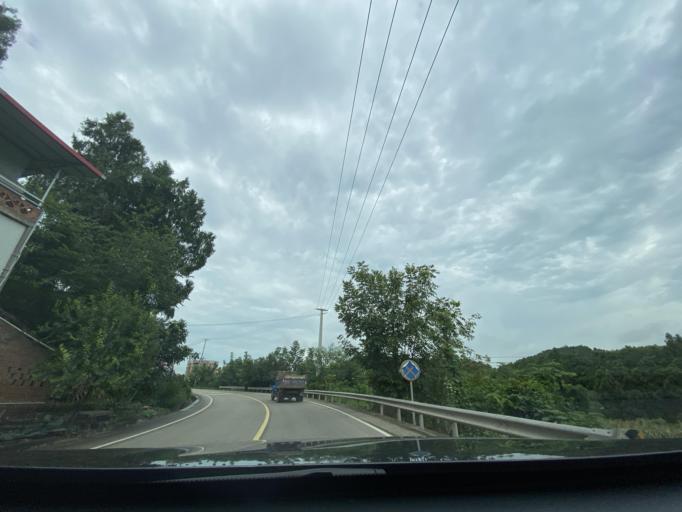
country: CN
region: Sichuan
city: Jiancheng
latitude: 30.4289
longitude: 104.6379
